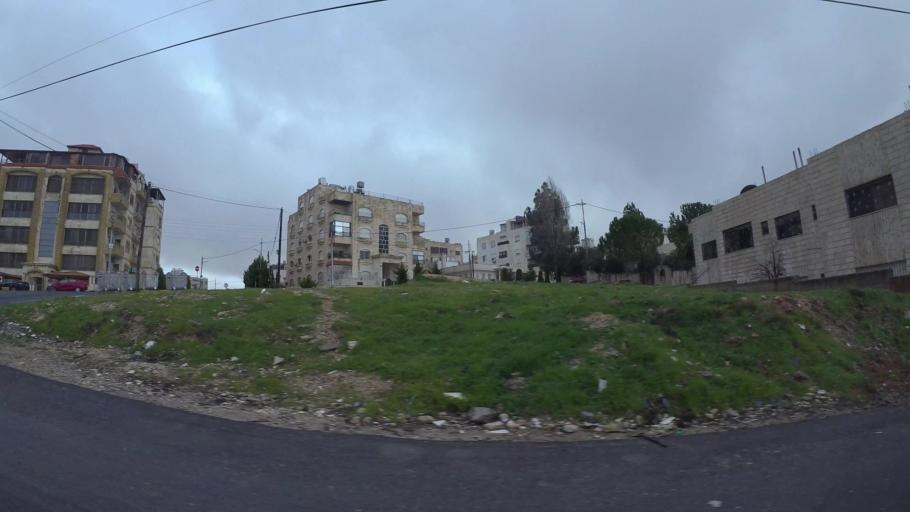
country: JO
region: Amman
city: Al Jubayhah
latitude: 32.0313
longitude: 35.8552
